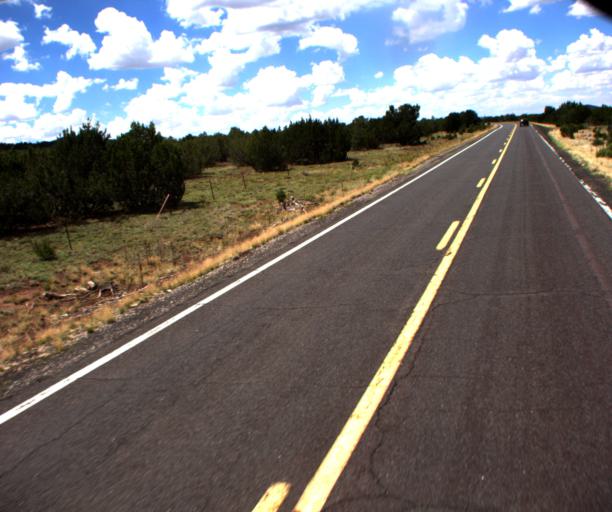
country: US
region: Arizona
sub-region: Coconino County
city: Parks
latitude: 35.5624
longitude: -111.8833
